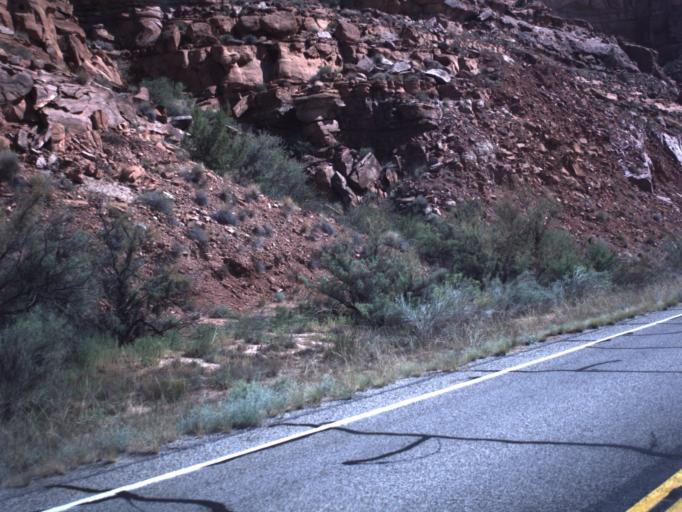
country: US
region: Utah
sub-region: Grand County
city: Moab
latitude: 38.5507
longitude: -109.6313
